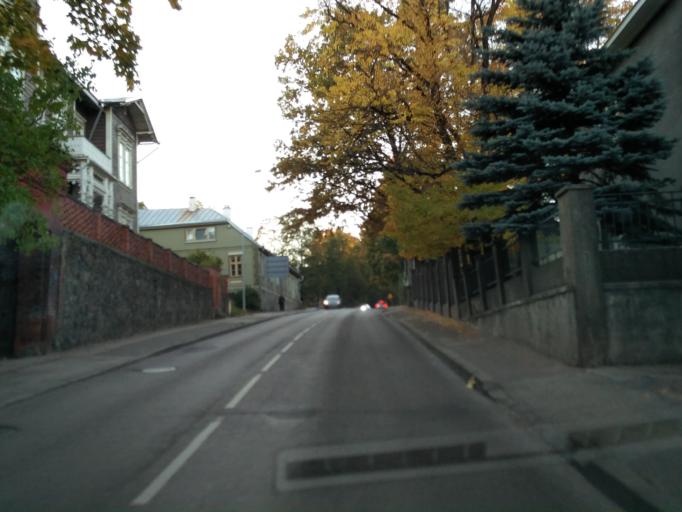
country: EE
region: Tartu
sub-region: Tartu linn
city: Tartu
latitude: 58.3827
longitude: 26.7130
